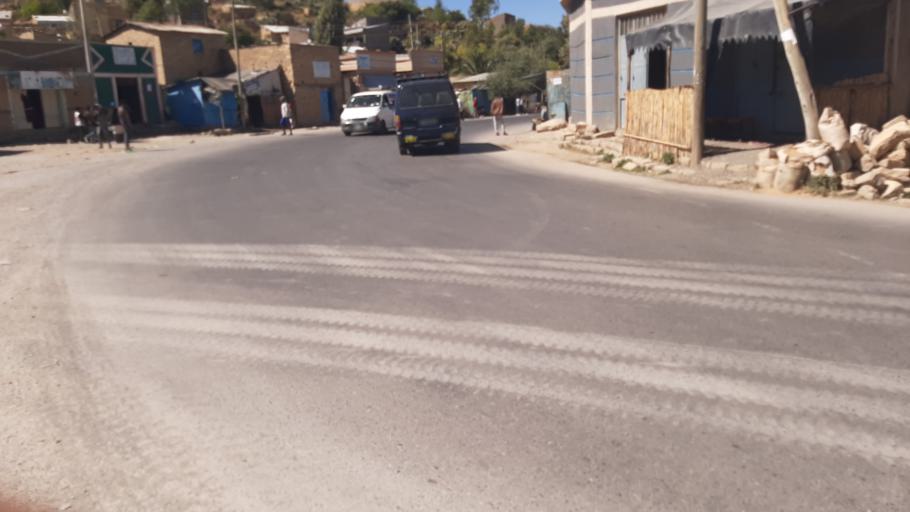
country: ET
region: Tigray
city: Mekele
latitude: 13.5824
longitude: 39.5681
